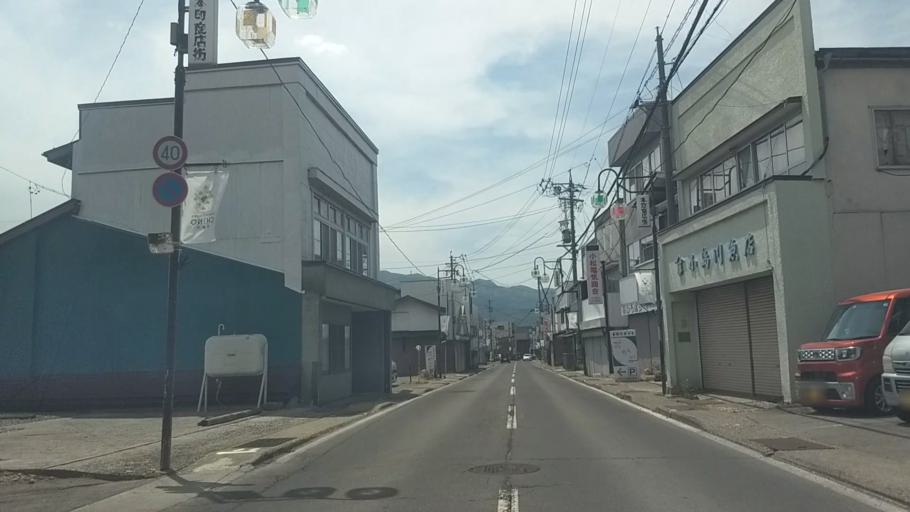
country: JP
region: Nagano
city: Chino
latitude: 35.9971
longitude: 138.1676
